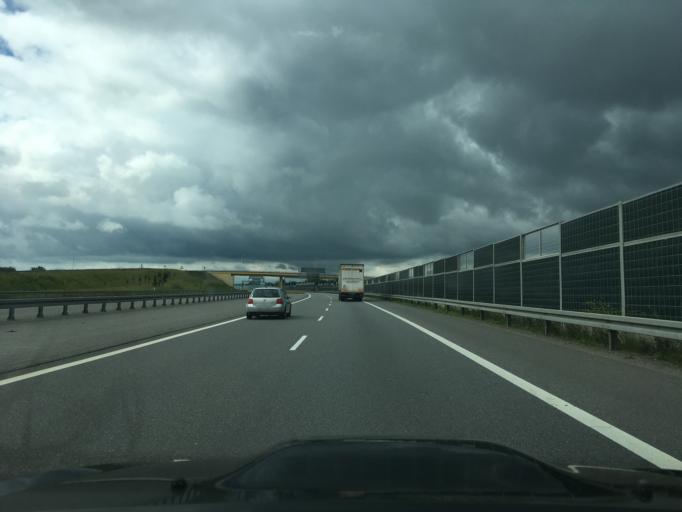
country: PL
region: Lublin Voivodeship
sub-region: Powiat lubelski
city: Jakubowice Murowane
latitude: 51.2946
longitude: 22.6081
